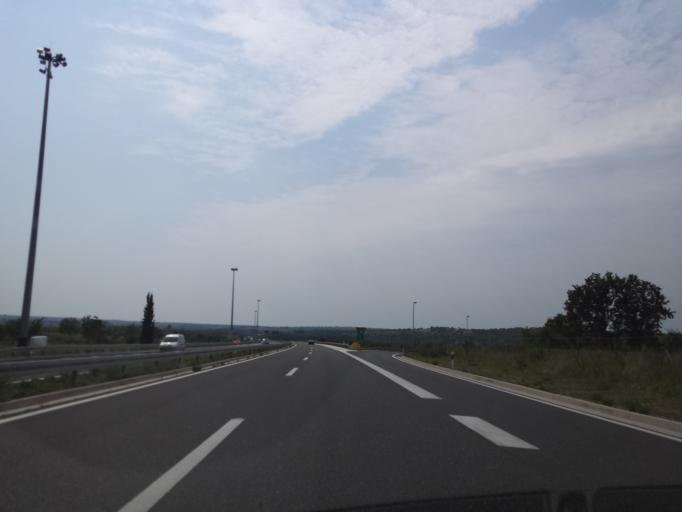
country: HR
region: Zadarska
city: Posedarje
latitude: 44.1892
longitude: 15.4343
